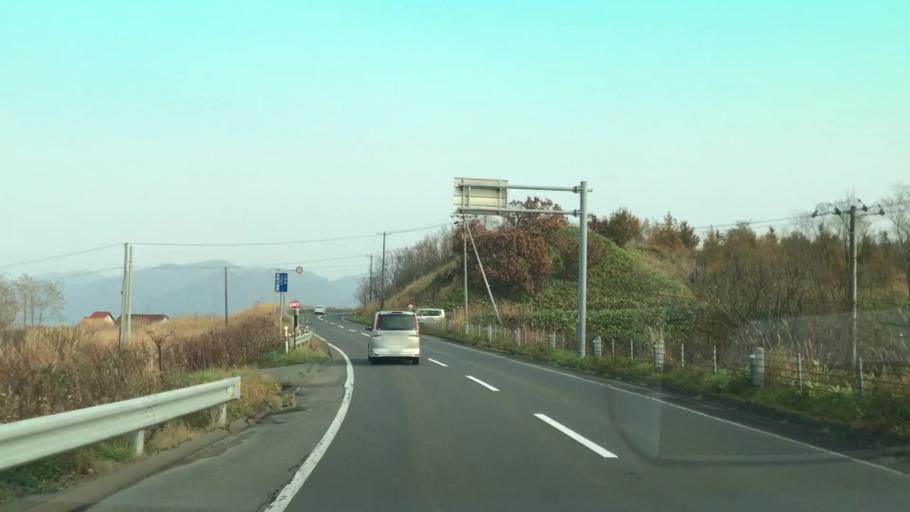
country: JP
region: Hokkaido
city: Ishikari
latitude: 43.3813
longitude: 141.4302
